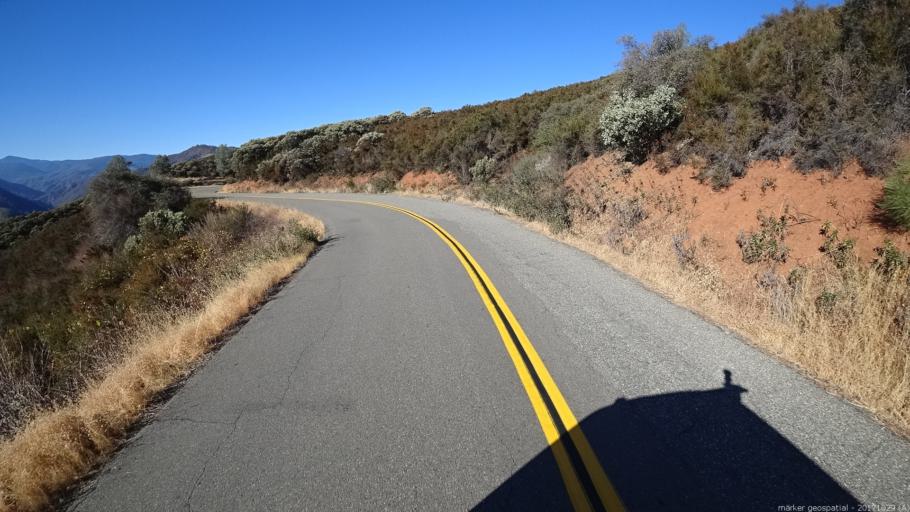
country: US
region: California
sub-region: Trinity County
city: Lewiston
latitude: 40.3659
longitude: -122.8545
